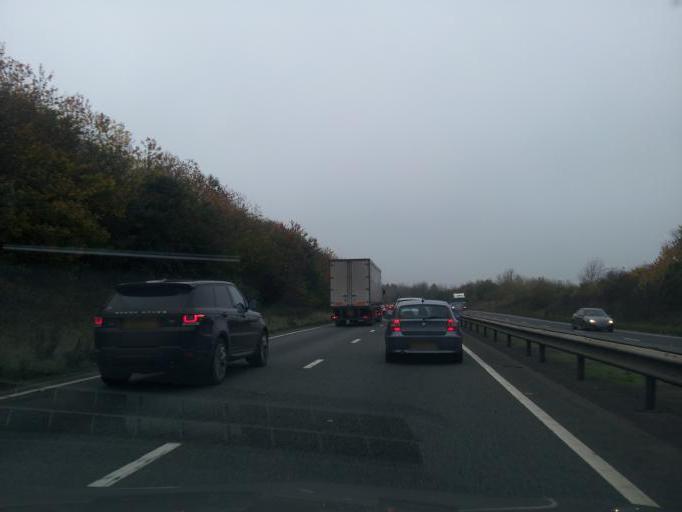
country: GB
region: England
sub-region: Leicestershire
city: Anstey
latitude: 52.6751
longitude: -1.1756
